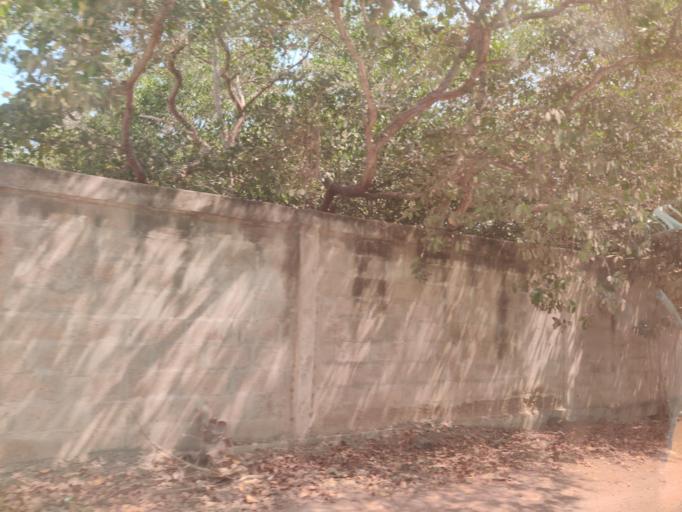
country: CO
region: Bolivar
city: Turbana
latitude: 10.1909
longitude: -75.6315
